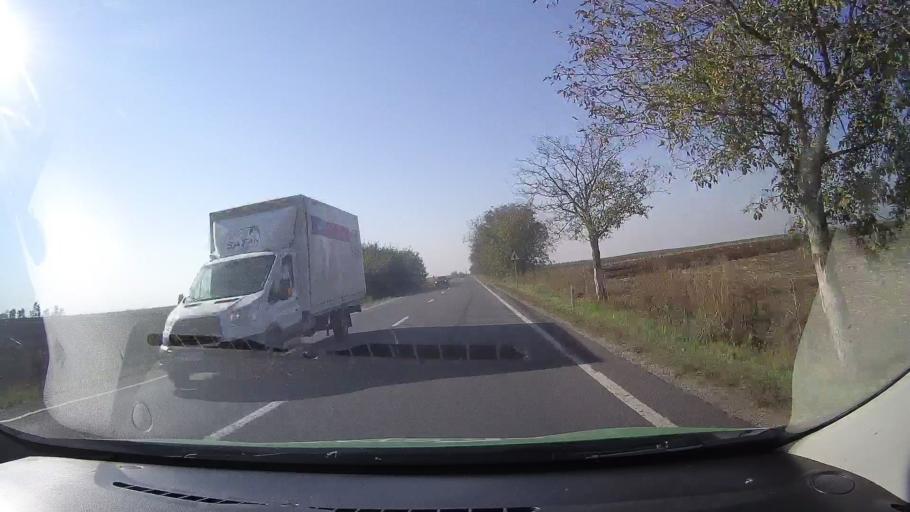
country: RO
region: Satu Mare
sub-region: Comuna Petresti
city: Petresti
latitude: 47.6263
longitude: 22.3881
